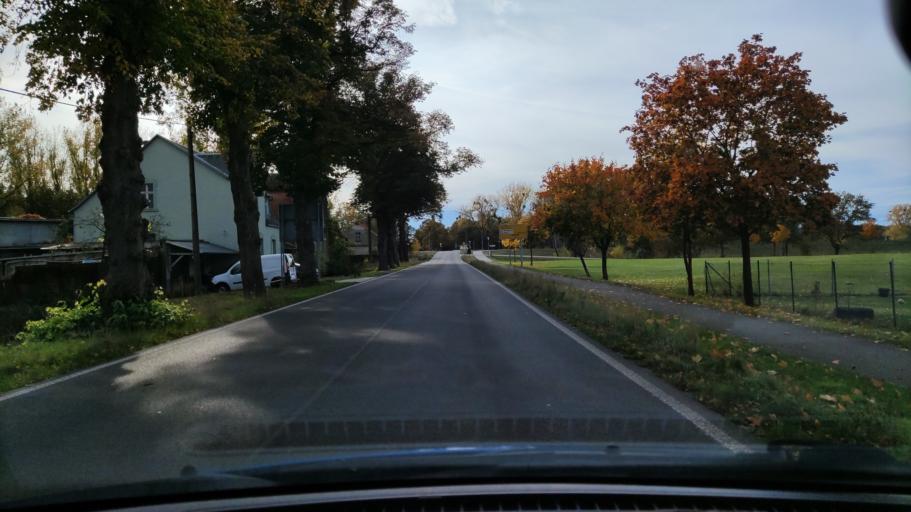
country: DE
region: Brandenburg
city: Breese
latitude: 53.0001
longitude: 11.7857
